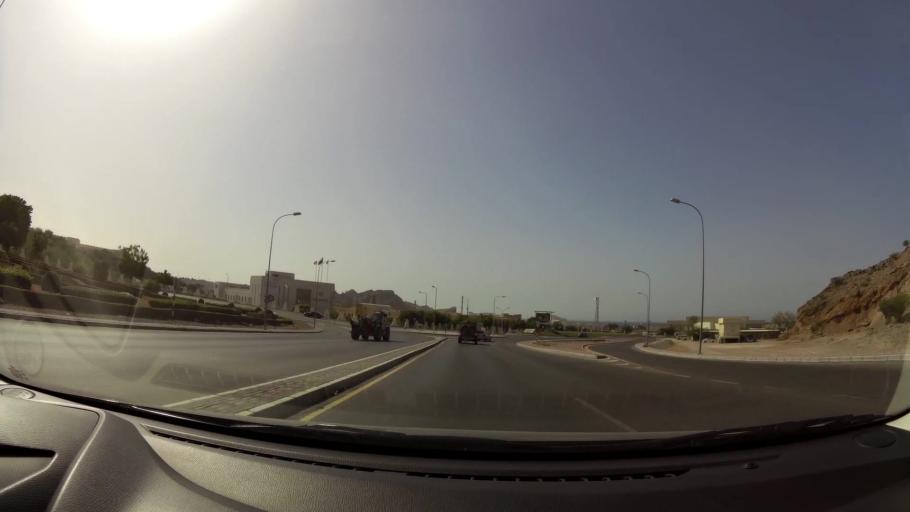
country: OM
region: Muhafazat Masqat
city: Muscat
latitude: 23.6190
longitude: 58.5194
